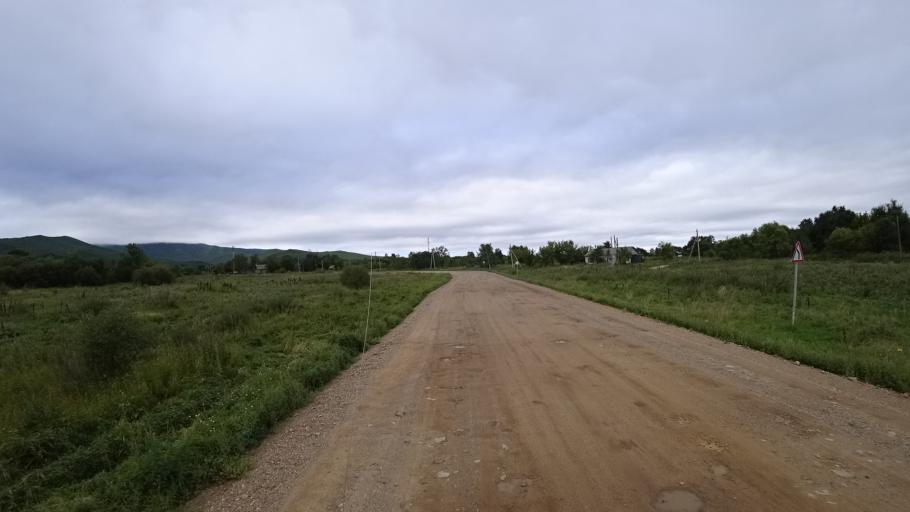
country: RU
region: Primorskiy
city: Rettikhovka
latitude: 44.1348
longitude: 132.6473
